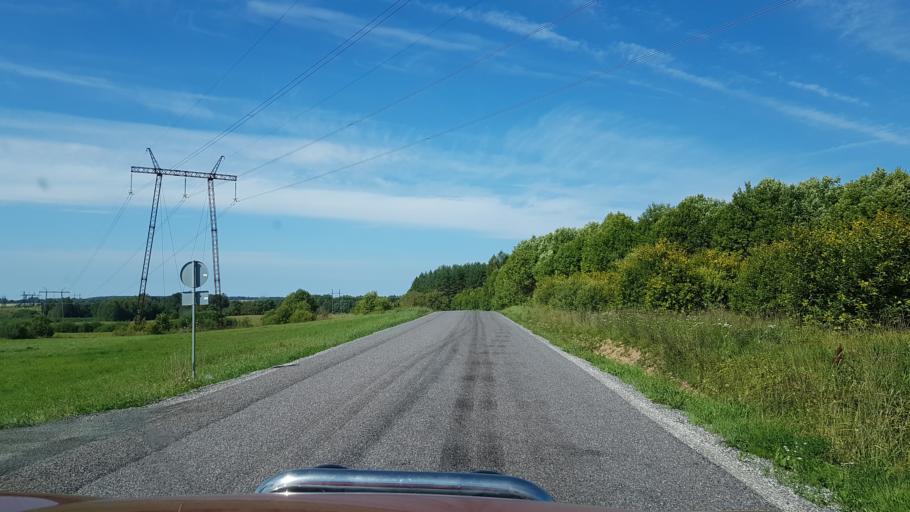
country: EE
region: Tartu
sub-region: Elva linn
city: Elva
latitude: 58.2438
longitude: 26.3961
